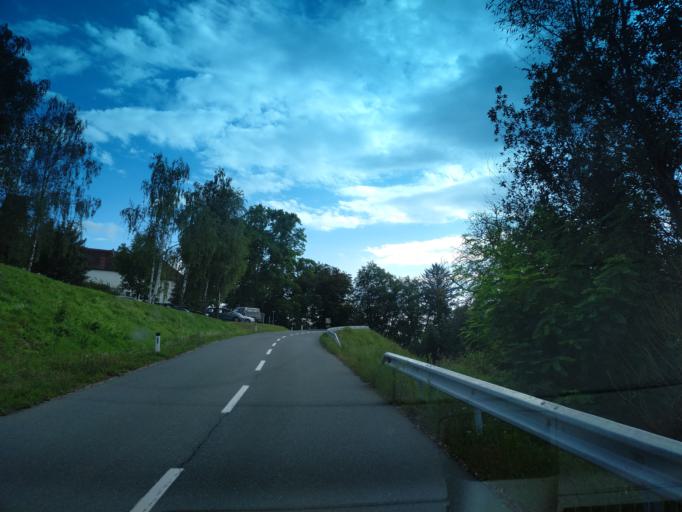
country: AT
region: Styria
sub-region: Politischer Bezirk Leibnitz
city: Leibnitz
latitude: 46.7824
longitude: 15.5228
